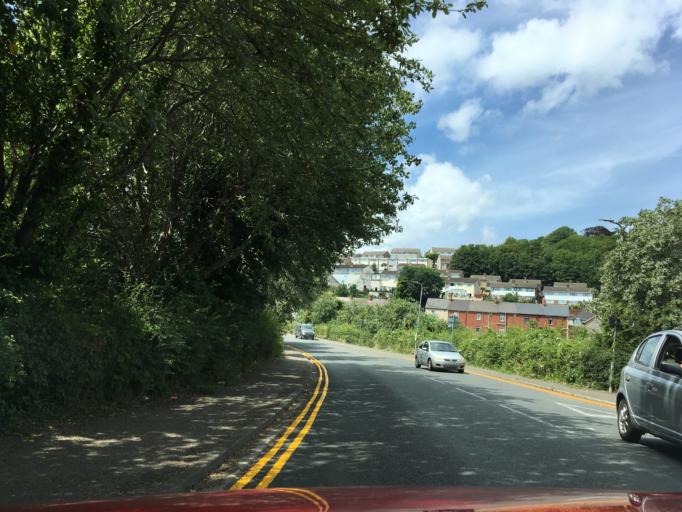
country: GB
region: Wales
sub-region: Newport
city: Caerleon
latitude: 51.5878
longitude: -2.9561
